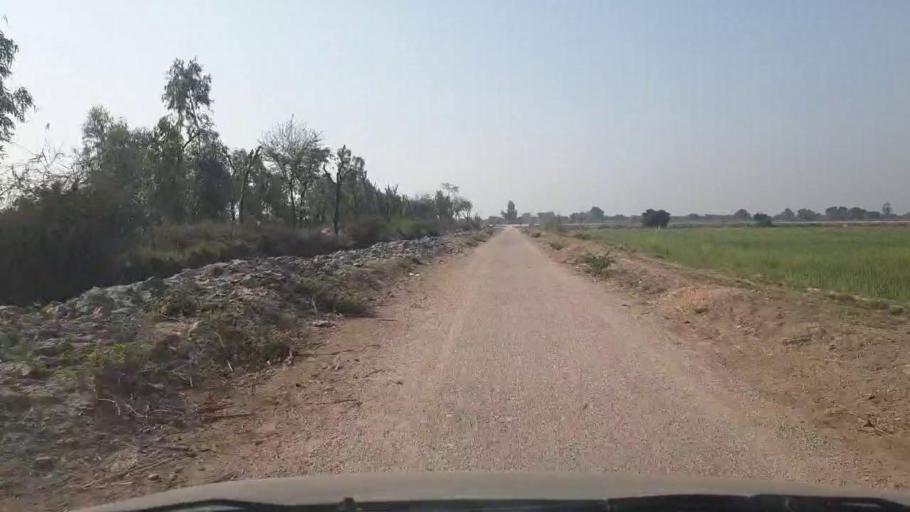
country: PK
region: Sindh
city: Mirwah Gorchani
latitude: 25.2621
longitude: 69.1136
